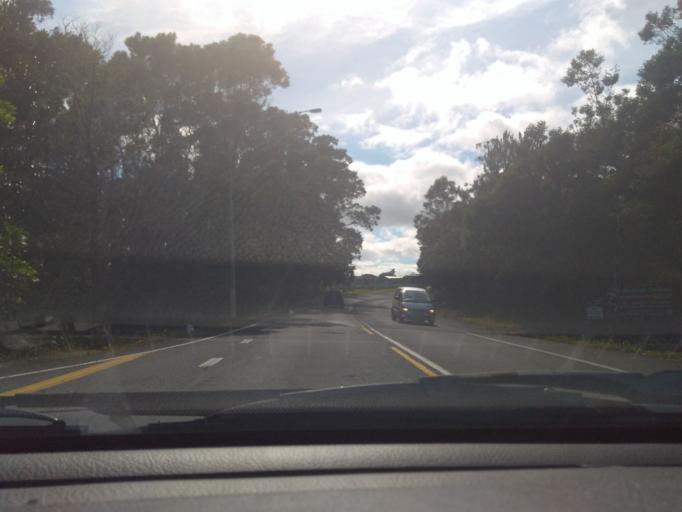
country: NZ
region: Northland
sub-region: Far North District
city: Taipa
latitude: -34.9933
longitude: 173.5268
